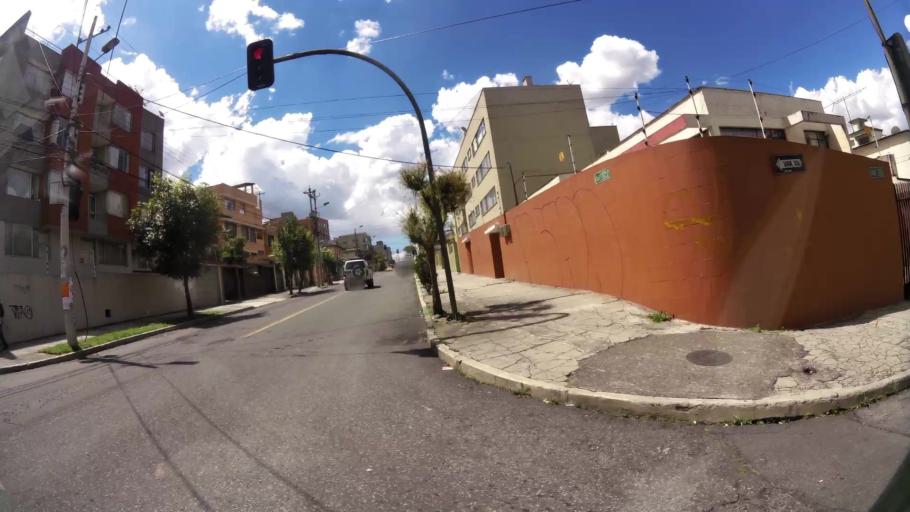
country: EC
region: Pichincha
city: Quito
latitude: -0.1916
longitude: -78.5000
